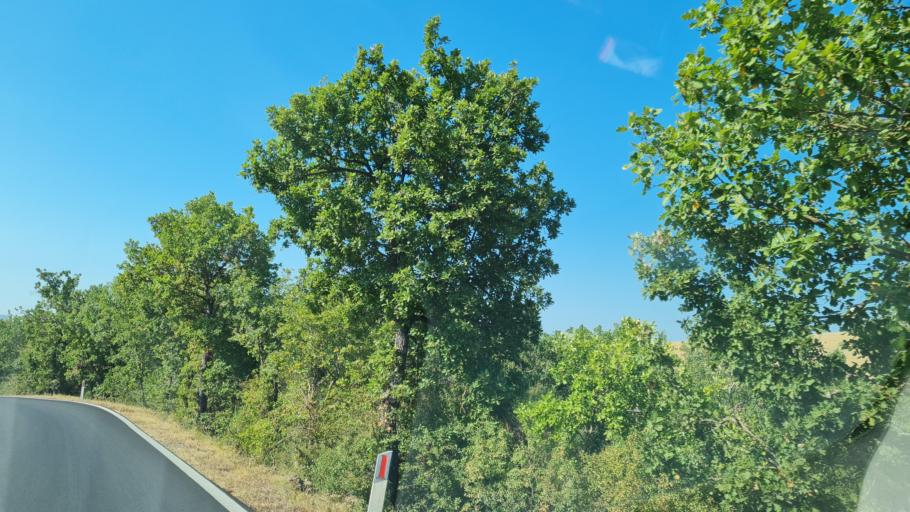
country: IT
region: Tuscany
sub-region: Provincia di Siena
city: Chianciano Terme
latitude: 43.0189
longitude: 11.7664
